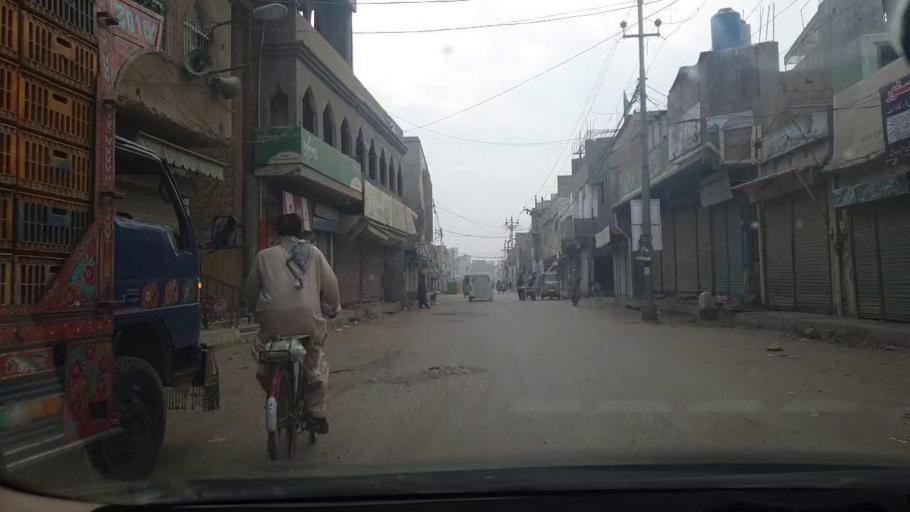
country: PK
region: Sindh
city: Malir Cantonment
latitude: 24.8788
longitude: 67.1913
